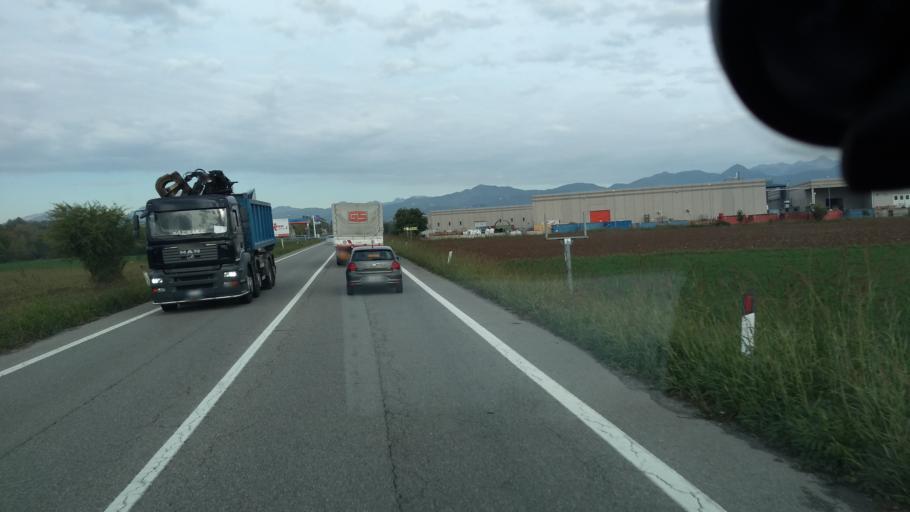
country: IT
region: Lombardy
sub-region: Provincia di Bergamo
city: Grassobbio
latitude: 45.6437
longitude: 9.7089
